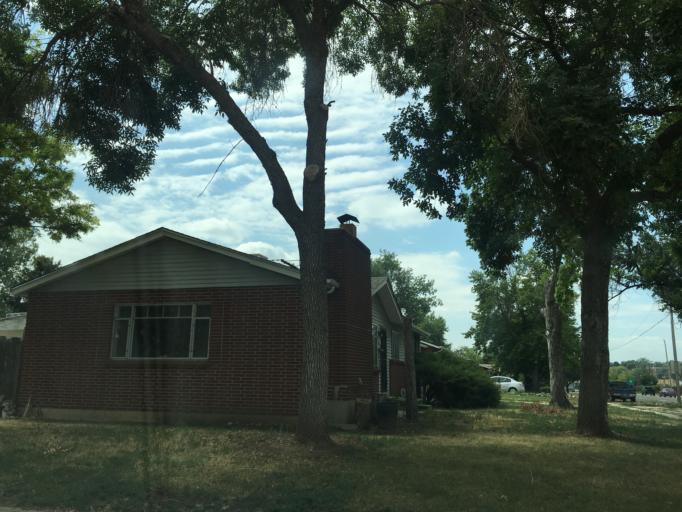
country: US
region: Colorado
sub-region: Arapahoe County
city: Sheridan
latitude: 39.6597
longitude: -105.0528
